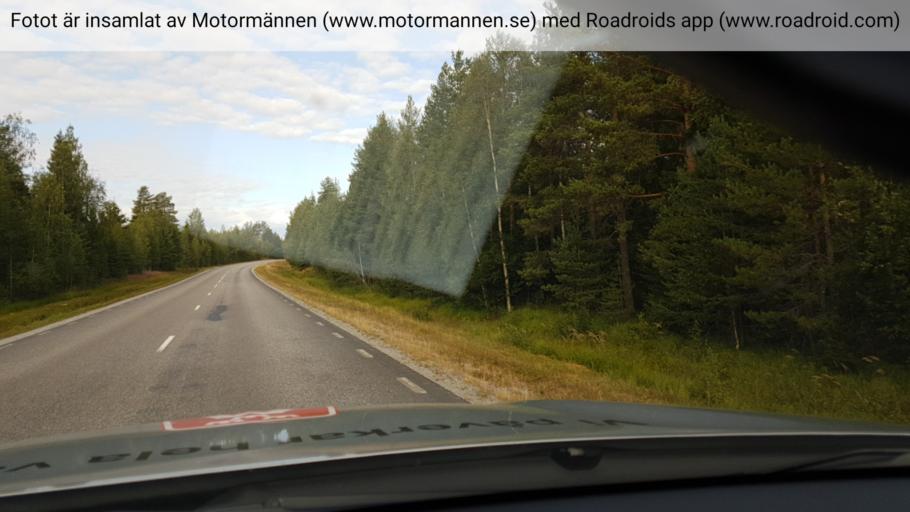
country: SE
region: Norrbotten
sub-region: Pitea Kommun
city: Roknas
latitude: 65.3399
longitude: 21.1604
